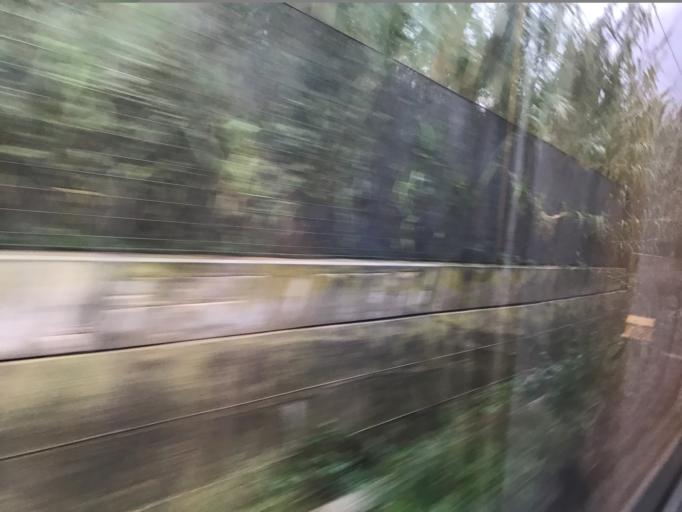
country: IT
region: Latium
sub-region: Citta metropolitana di Roma Capitale
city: Vitinia
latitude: 41.8337
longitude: 12.4423
